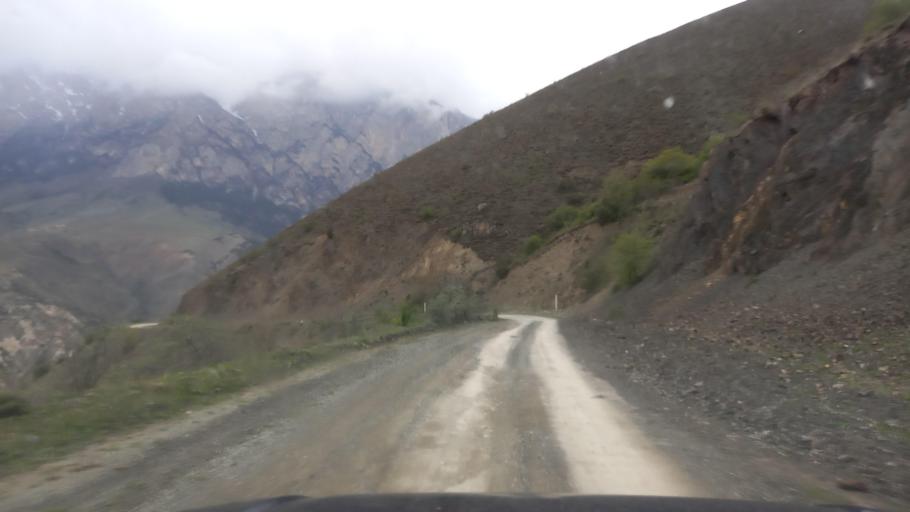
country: RU
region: North Ossetia
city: Mizur
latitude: 42.8548
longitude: 44.1615
